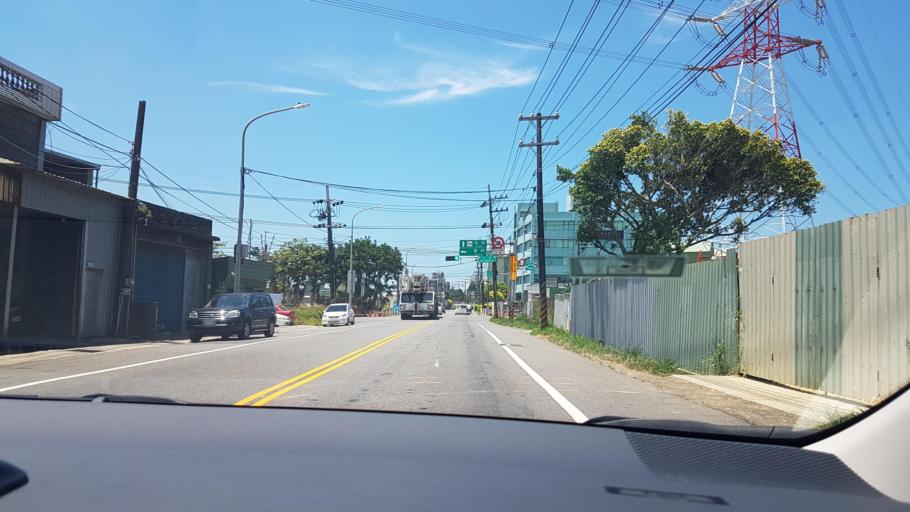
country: TW
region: Taiwan
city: Taoyuan City
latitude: 25.0904
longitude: 121.2753
